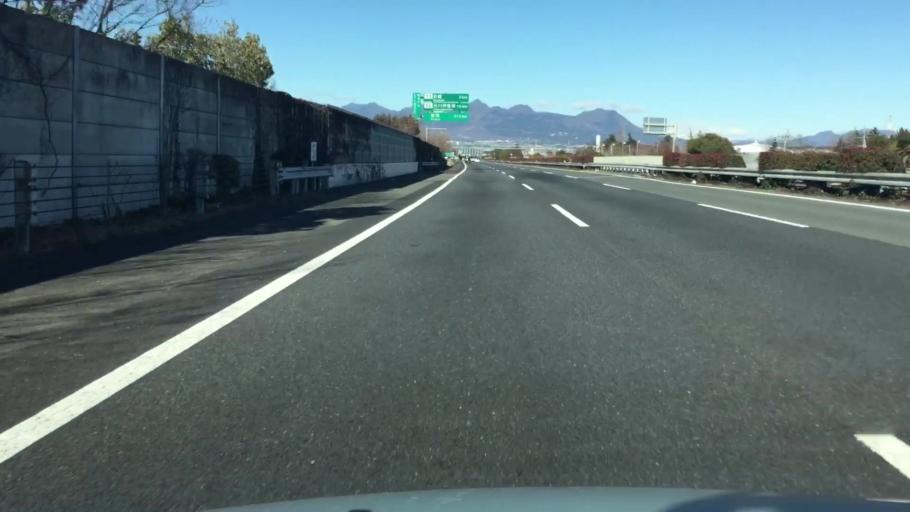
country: JP
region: Gunma
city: Takasaki
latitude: 36.3461
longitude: 139.0521
